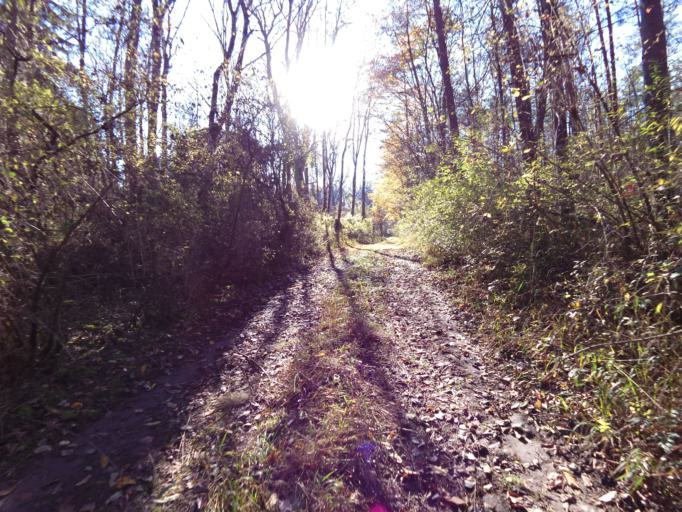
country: DE
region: Bavaria
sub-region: Upper Bavaria
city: Wang
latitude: 48.5033
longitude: 11.9809
